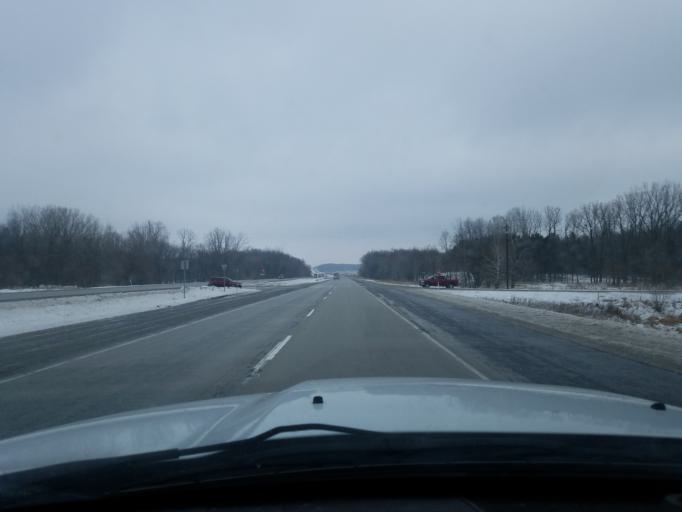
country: US
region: Indiana
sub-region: Fulton County
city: Rochester
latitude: 41.0908
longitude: -86.2405
